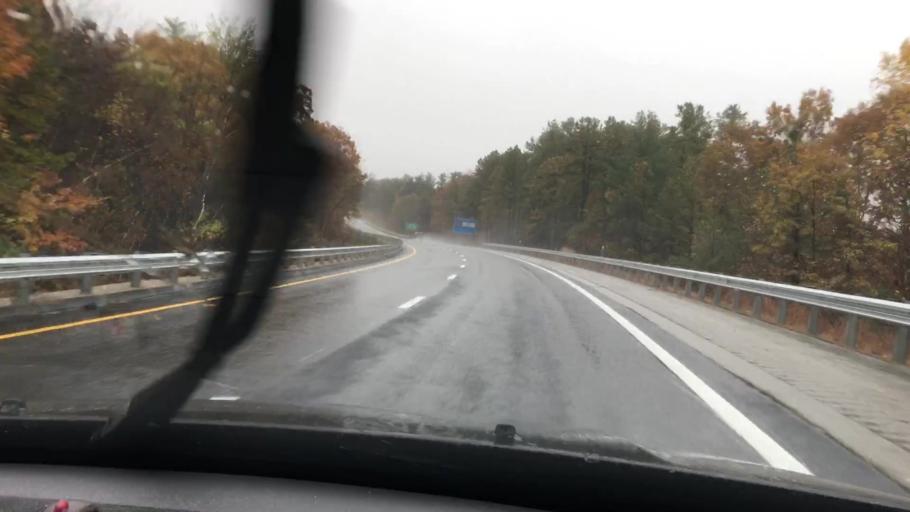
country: US
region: New Hampshire
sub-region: Merrimack County
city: Boscawen
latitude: 43.3379
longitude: -71.6153
